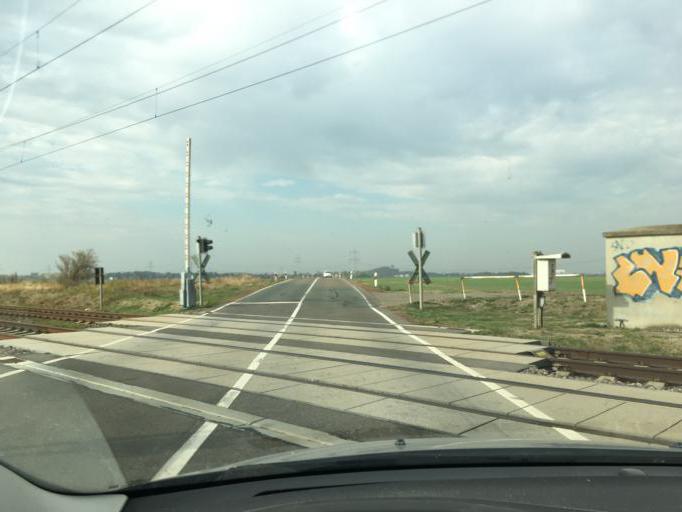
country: DE
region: Saxony
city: Wiedemar
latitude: 51.5048
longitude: 12.1929
